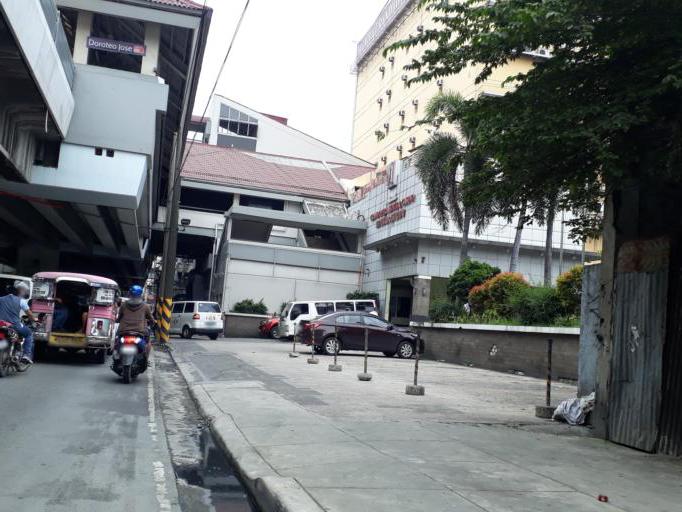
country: PH
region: Metro Manila
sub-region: City of Manila
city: Manila
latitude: 14.6061
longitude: 120.9821
